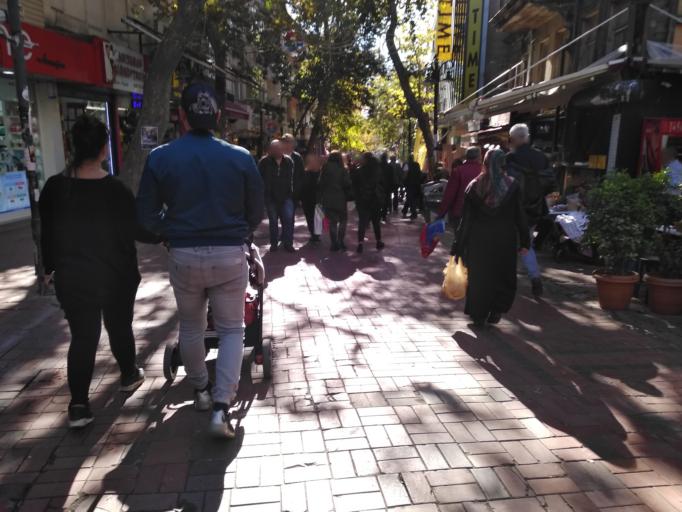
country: TR
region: Istanbul
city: Maltepe
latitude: 40.9240
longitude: 29.1308
